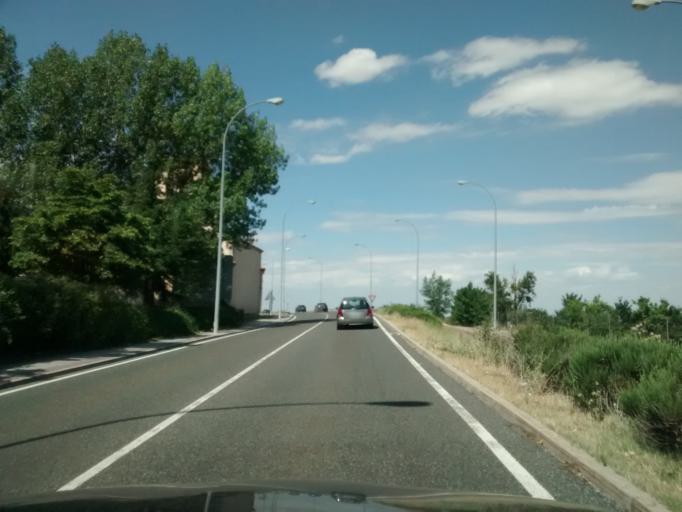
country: ES
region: Castille and Leon
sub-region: Provincia de Segovia
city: Torrecaballeros
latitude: 40.9937
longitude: -4.0240
